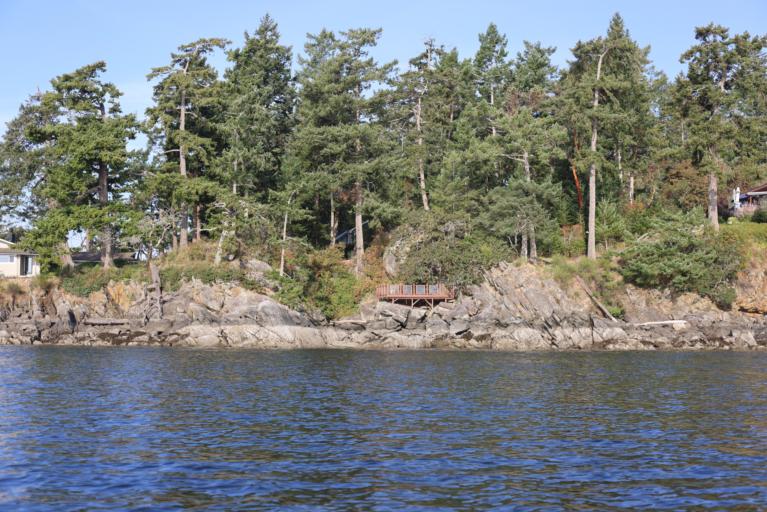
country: CA
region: British Columbia
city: North Saanich
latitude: 48.6752
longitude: -123.3956
